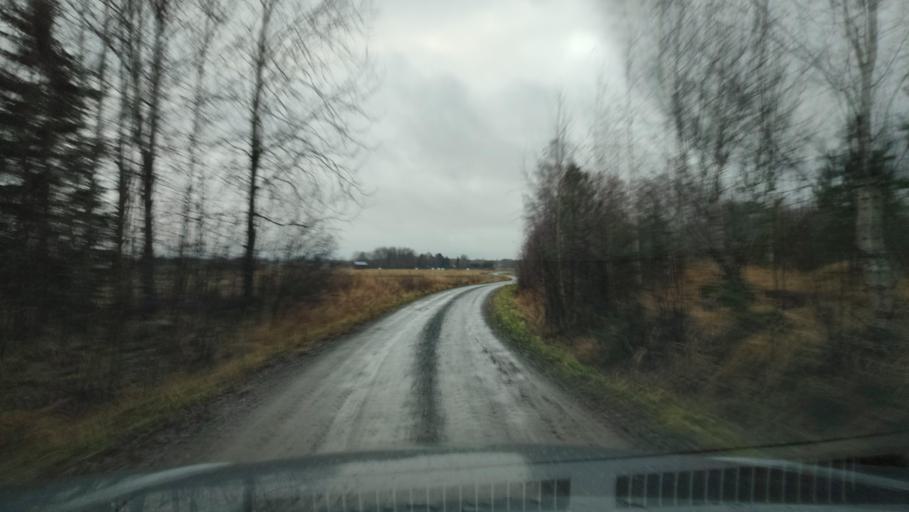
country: FI
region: Ostrobothnia
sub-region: Sydosterbotten
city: Kristinestad
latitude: 62.2432
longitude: 21.4876
